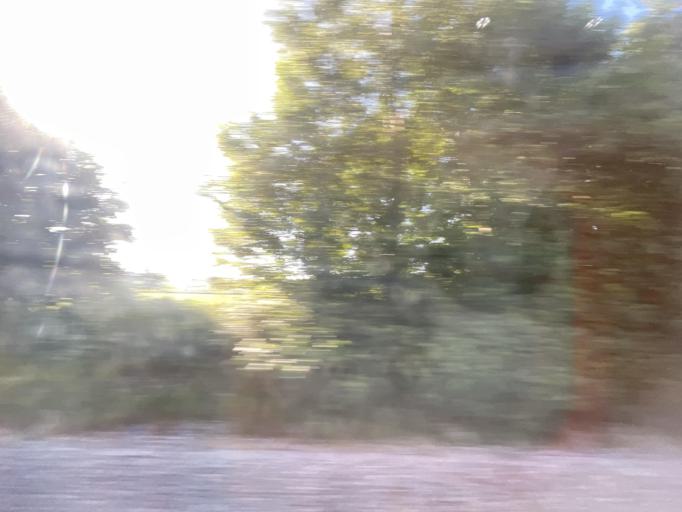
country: GB
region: Wales
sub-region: Gwynedd
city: Aber
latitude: 53.2289
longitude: -4.0524
